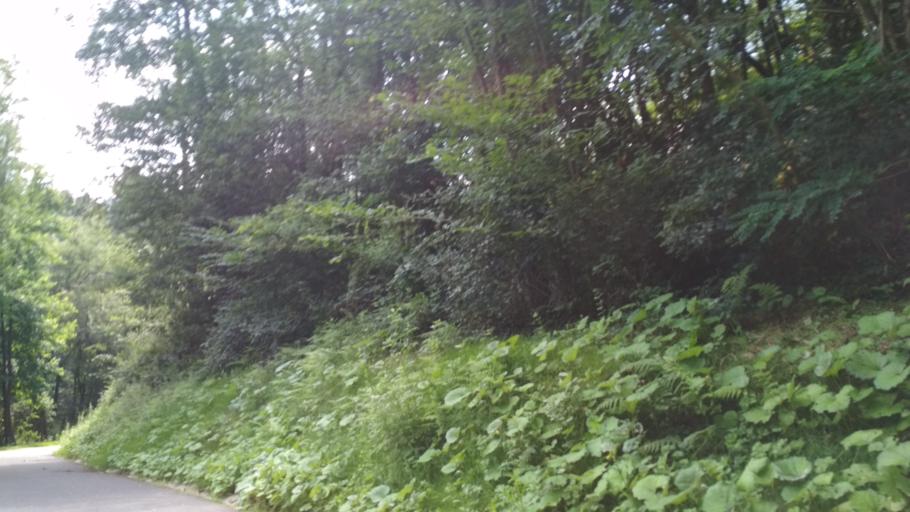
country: ES
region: Basque Country
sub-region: Provincia de Guipuzcoa
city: San Sebastian
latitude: 43.2963
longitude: -1.9837
